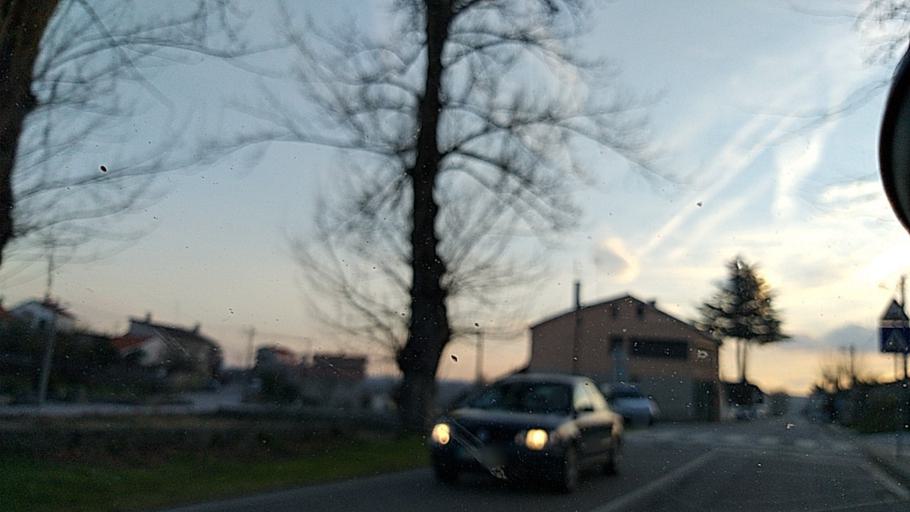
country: PT
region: Guarda
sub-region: Guarda
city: Sequeira
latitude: 40.5783
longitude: -7.1770
